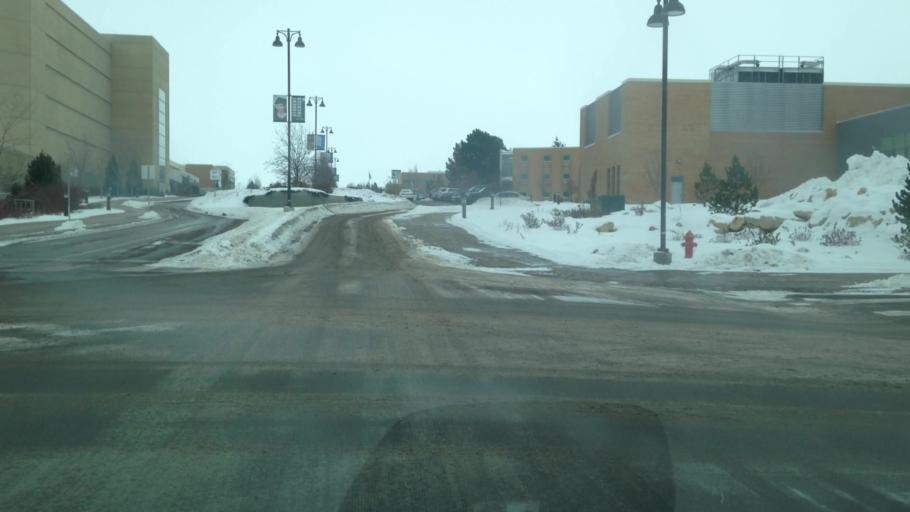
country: US
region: Idaho
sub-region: Madison County
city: Rexburg
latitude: 43.8177
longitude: -111.7868
